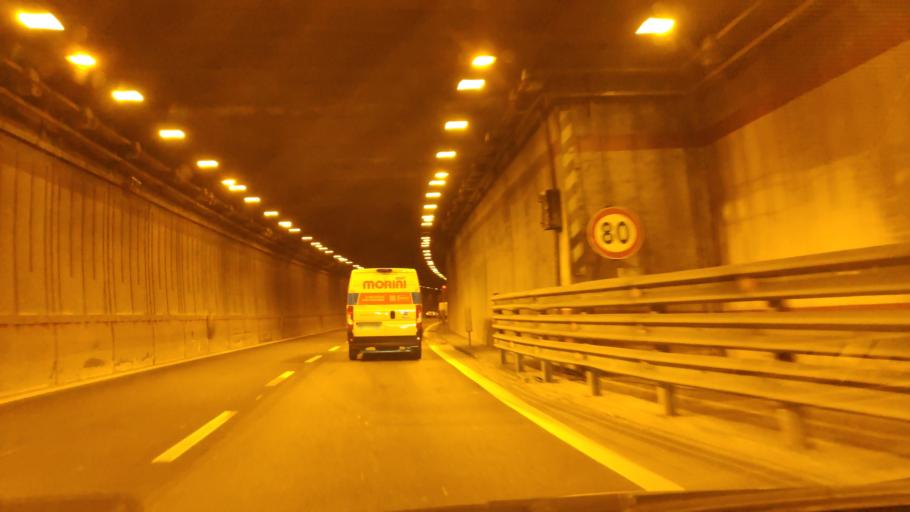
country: IT
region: Lombardy
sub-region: Provincia di Monza e Brianza
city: Monza
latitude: 45.5574
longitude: 9.2613
